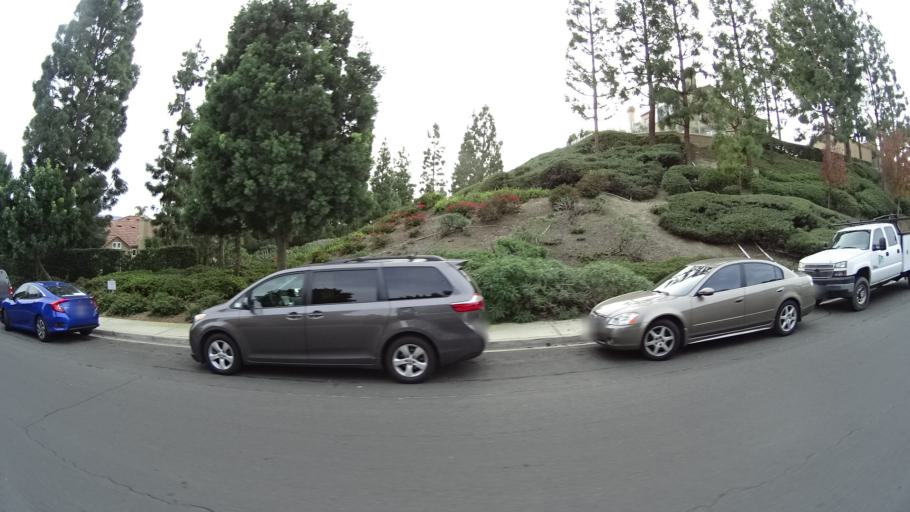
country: US
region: California
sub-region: Orange County
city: Laguna Woods
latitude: 33.5984
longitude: -117.7196
